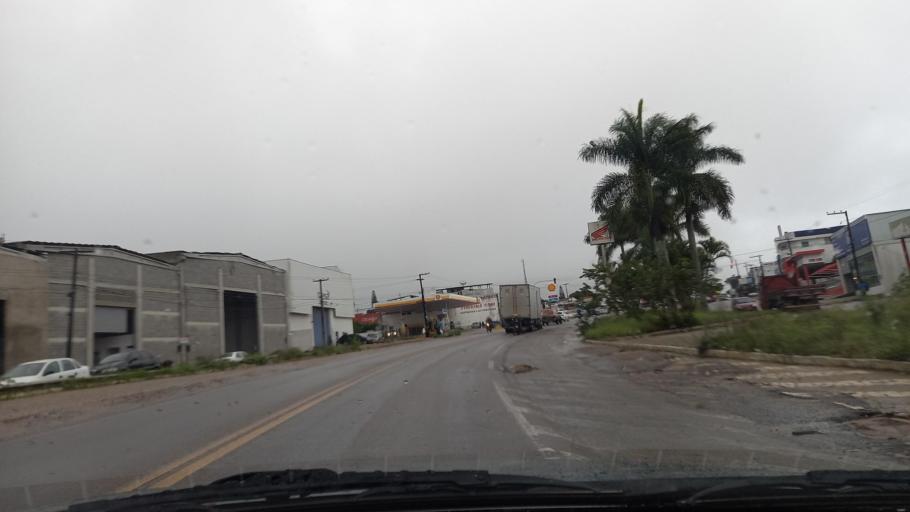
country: BR
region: Pernambuco
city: Garanhuns
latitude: -8.8820
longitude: -36.4890
